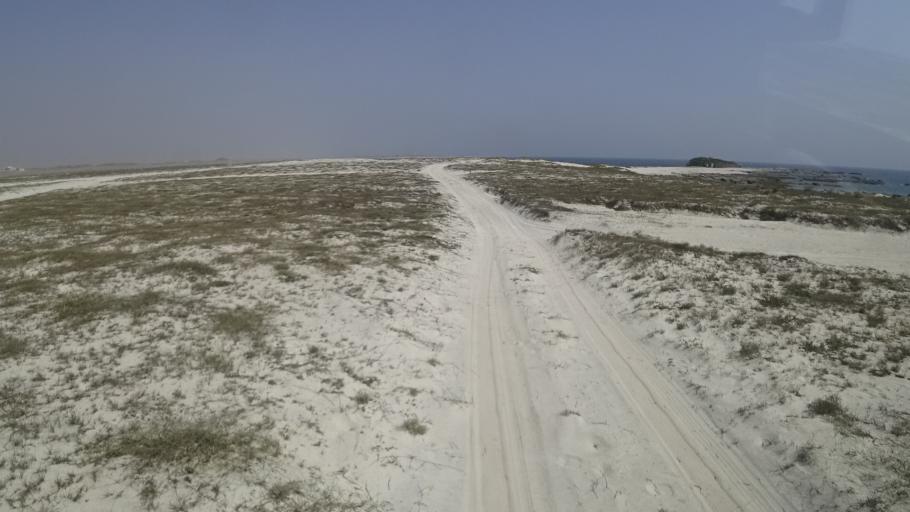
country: OM
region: Zufar
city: Salalah
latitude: 16.9700
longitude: 54.7041
